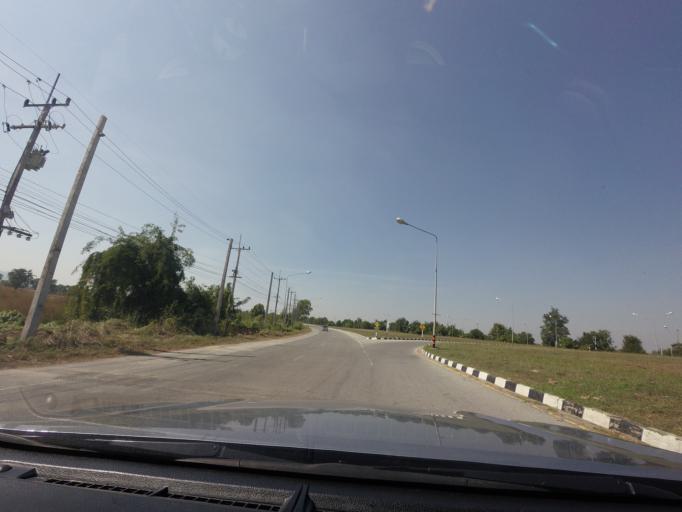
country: TH
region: Sukhothai
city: Ban Na
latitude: 17.0569
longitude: 99.7163
